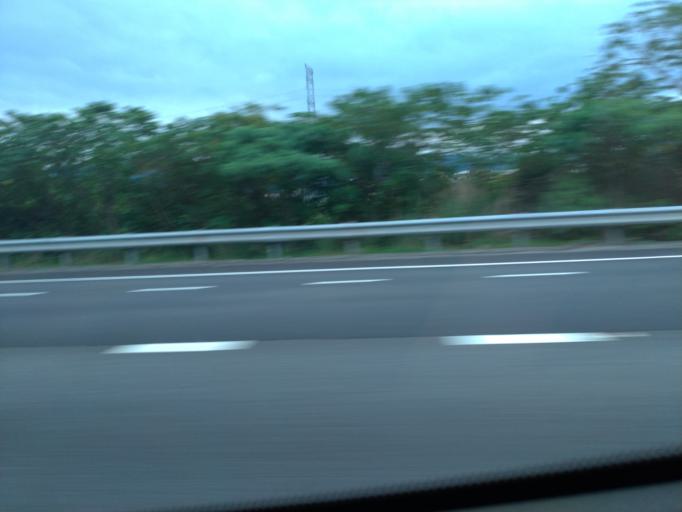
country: TW
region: Taiwan
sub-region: Taoyuan
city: Taoyuan
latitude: 24.9364
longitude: 121.3185
